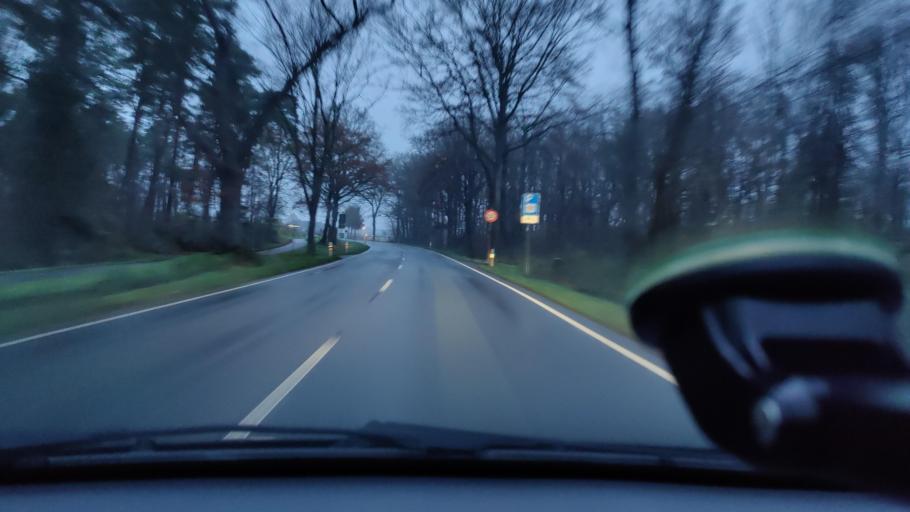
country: DE
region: North Rhine-Westphalia
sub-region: Regierungsbezirk Dusseldorf
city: Sonsbeck
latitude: 51.5935
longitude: 6.3858
